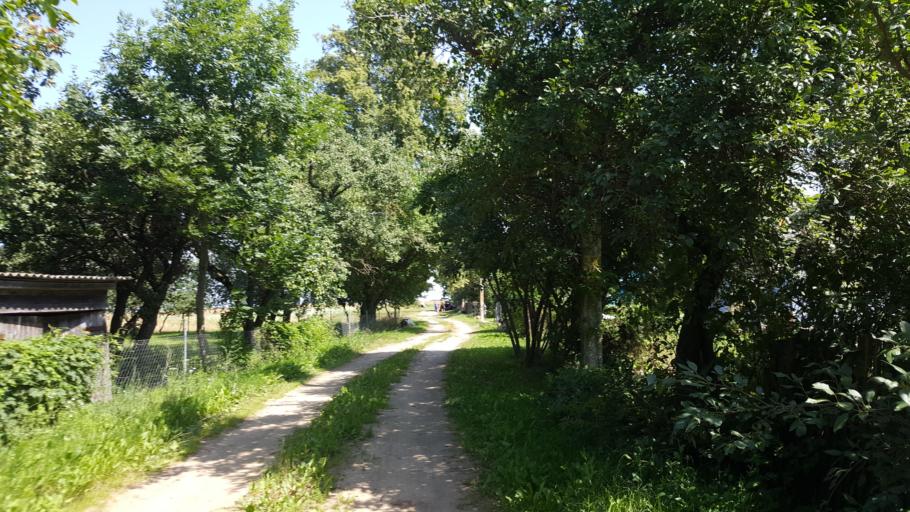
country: BY
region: Brest
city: Vysokaye
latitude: 52.3636
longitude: 23.5352
